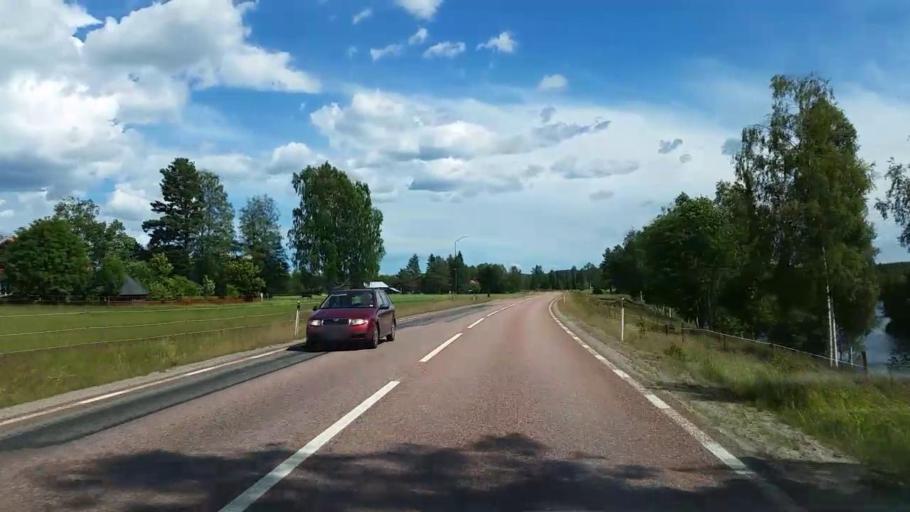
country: SE
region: Gaevleborg
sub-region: Ovanakers Kommun
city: Edsbyn
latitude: 61.3471
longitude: 15.6066
